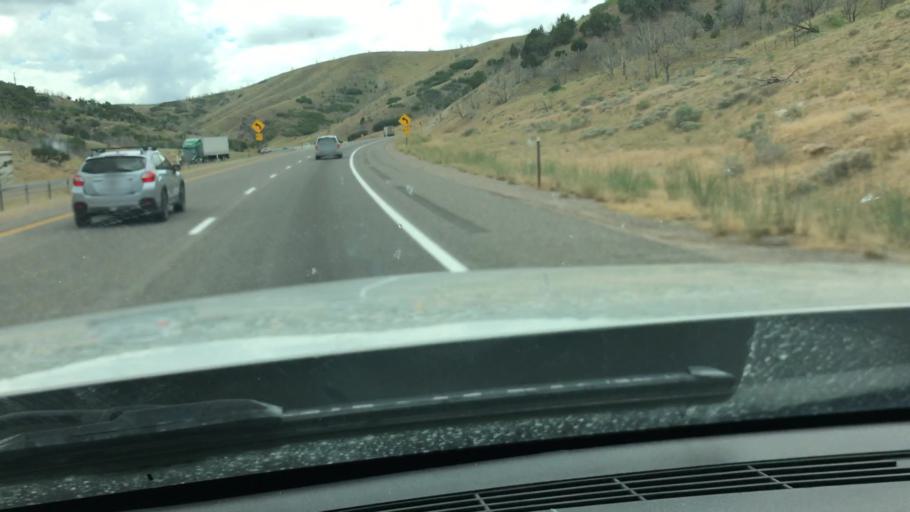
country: US
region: Utah
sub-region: Millard County
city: Fillmore
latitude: 38.6904
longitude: -112.6017
